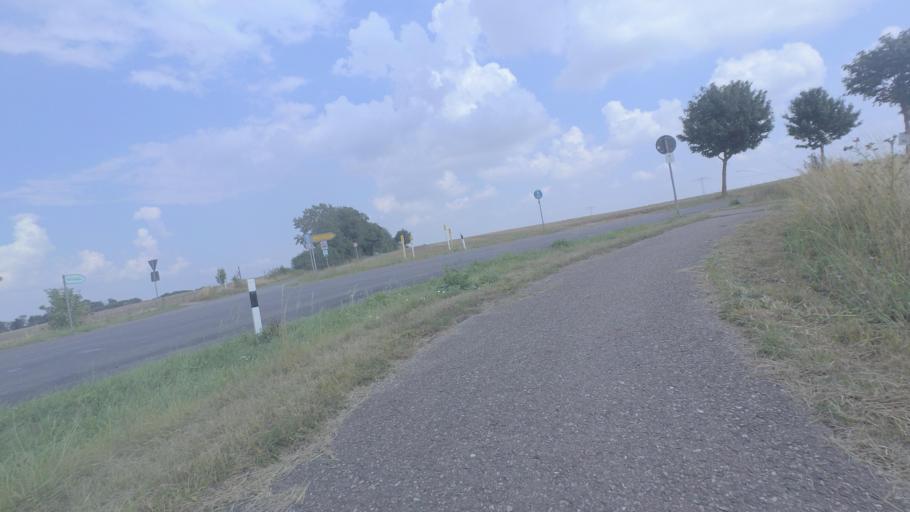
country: DE
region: Mecklenburg-Vorpommern
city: Neukalen
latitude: 53.7724
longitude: 12.8566
